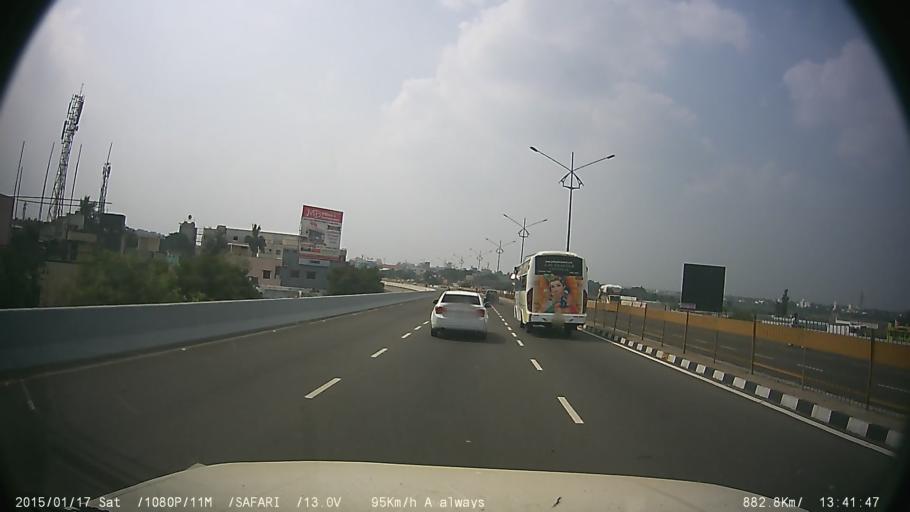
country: IN
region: Tamil Nadu
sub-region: Vellore
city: Vellore
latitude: 12.9348
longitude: 79.1490
